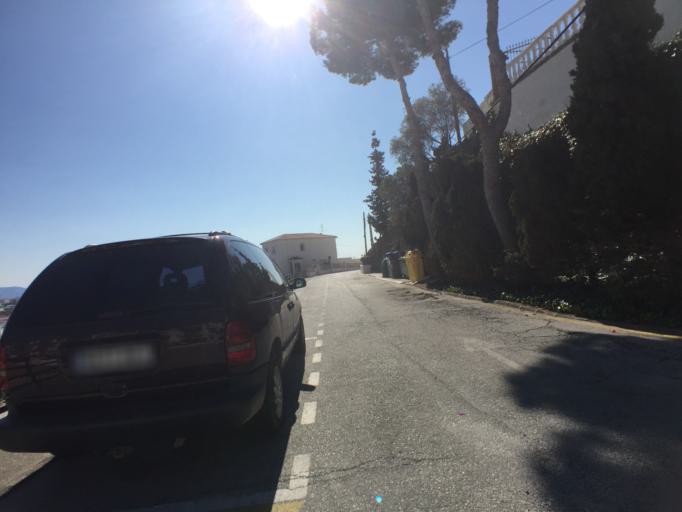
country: ES
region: Andalusia
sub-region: Provincia de Malaga
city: Nerja
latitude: 36.7462
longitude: -3.9062
